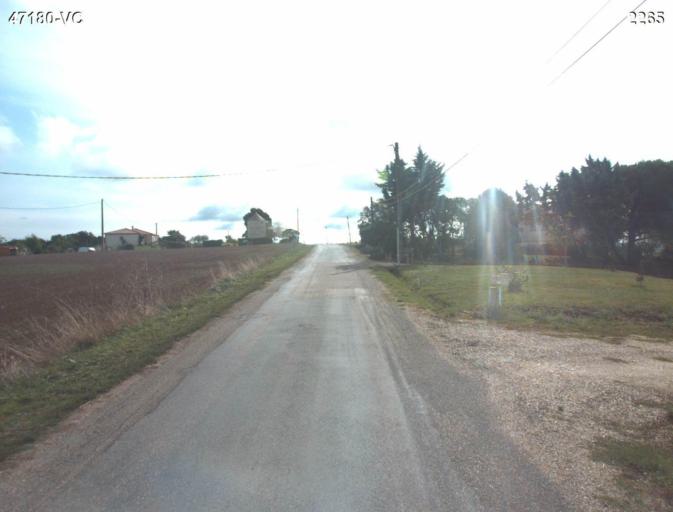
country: FR
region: Aquitaine
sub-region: Departement du Lot-et-Garonne
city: Sainte-Colombe-en-Bruilhois
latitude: 44.1711
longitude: 0.4430
